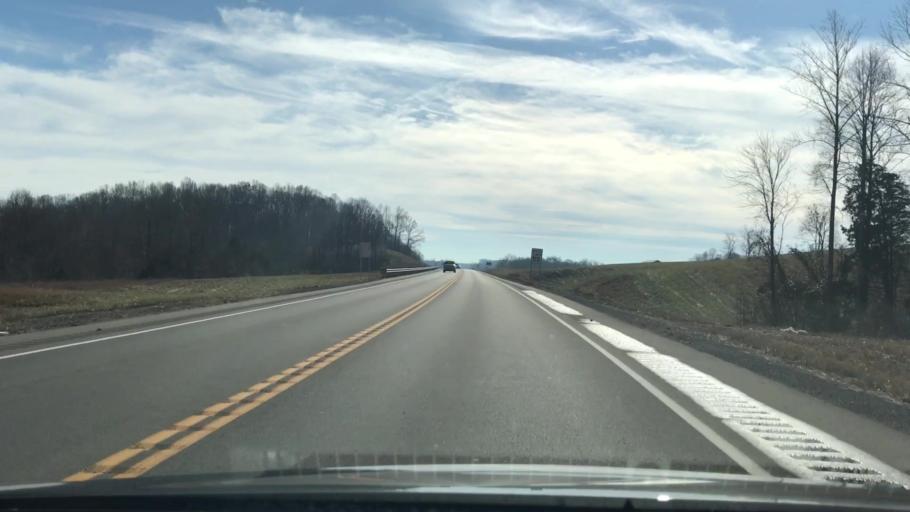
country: US
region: Kentucky
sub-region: Monroe County
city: Tompkinsville
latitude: 36.8204
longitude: -85.6885
